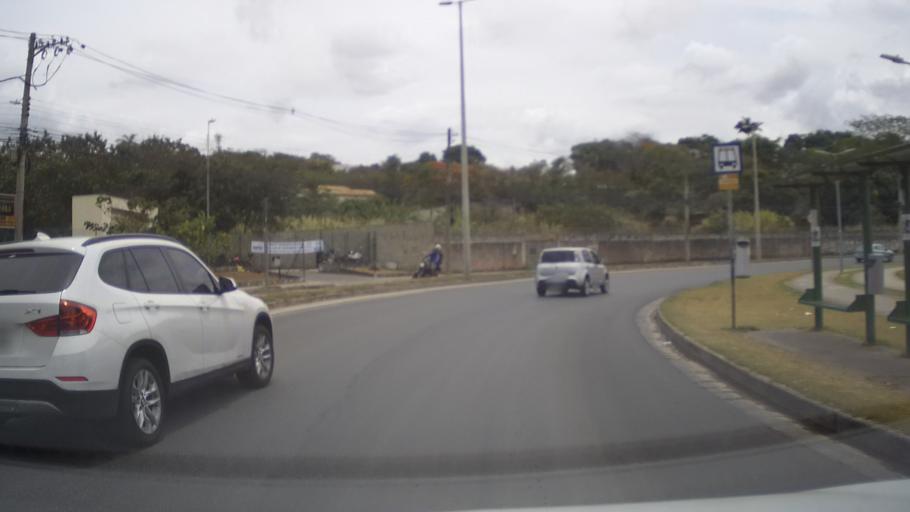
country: BR
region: Minas Gerais
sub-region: Contagem
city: Contagem
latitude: -19.8544
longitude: -44.0057
